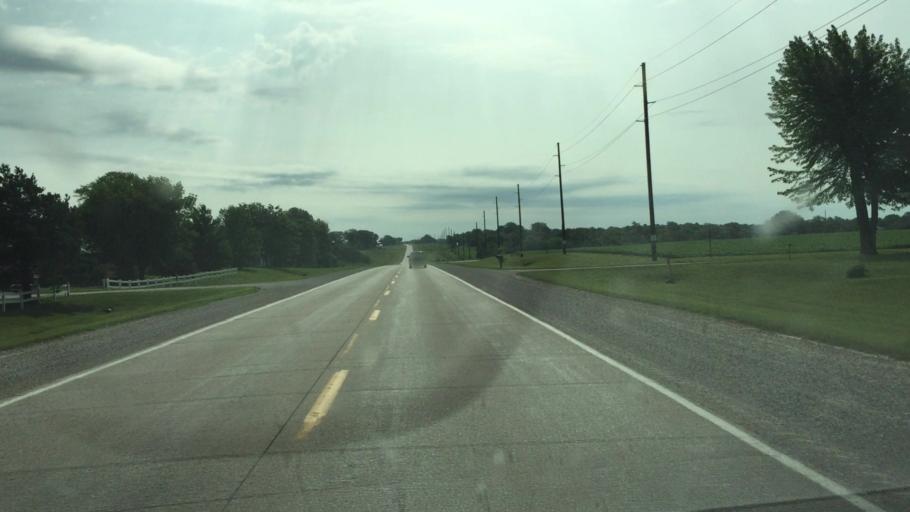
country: US
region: Illinois
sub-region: Hancock County
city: Nauvoo
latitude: 40.6390
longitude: -91.5500
